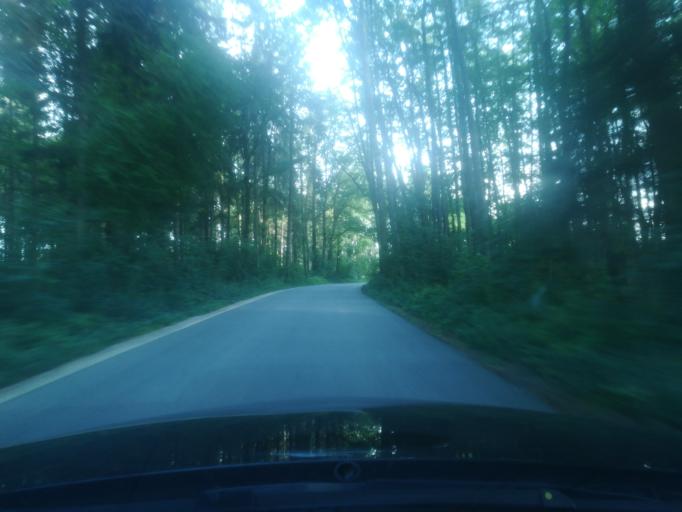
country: AT
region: Upper Austria
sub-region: Wels-Land
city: Marchtrenk
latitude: 48.1623
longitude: 14.1674
